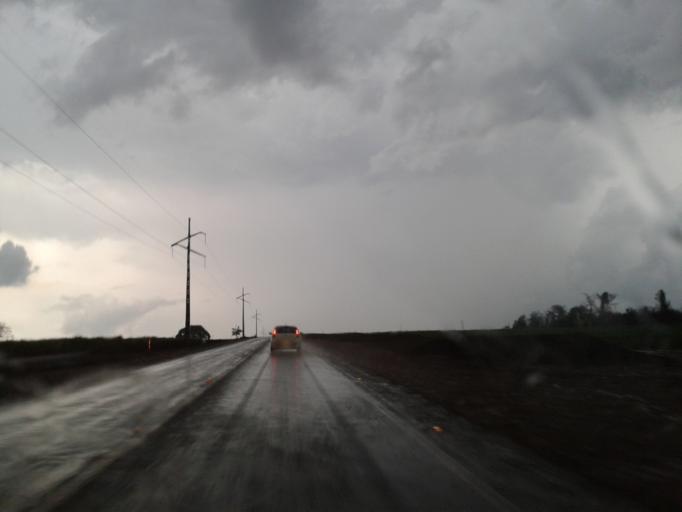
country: BR
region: Goias
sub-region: Quirinopolis
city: Quirinopolis
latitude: -18.5184
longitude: -50.4405
